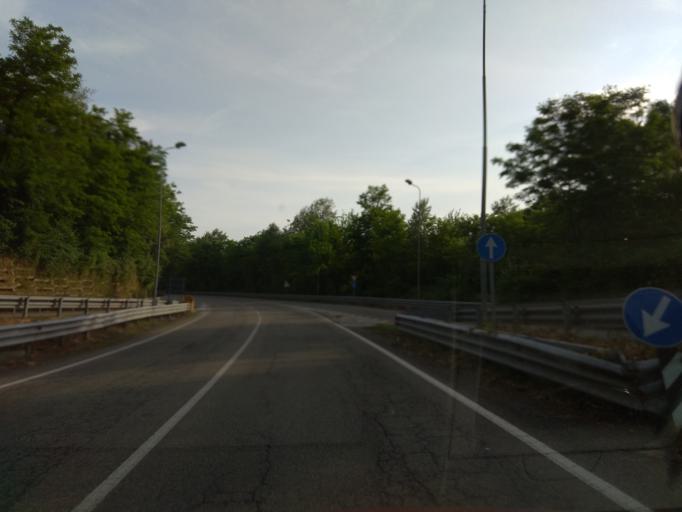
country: IT
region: Piedmont
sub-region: Provincia di Biella
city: Quaregna
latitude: 45.5765
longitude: 8.1696
